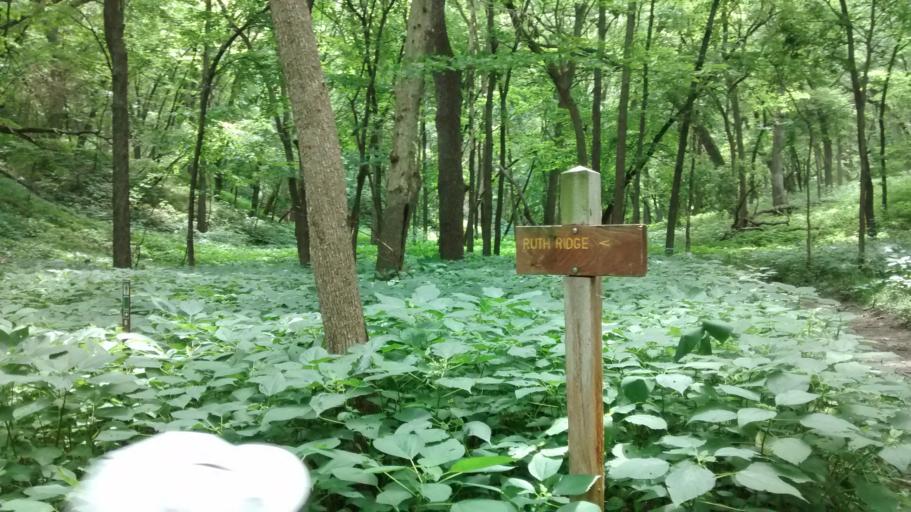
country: US
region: South Dakota
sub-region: Union County
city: North Sioux City
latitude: 42.5457
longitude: -96.4644
